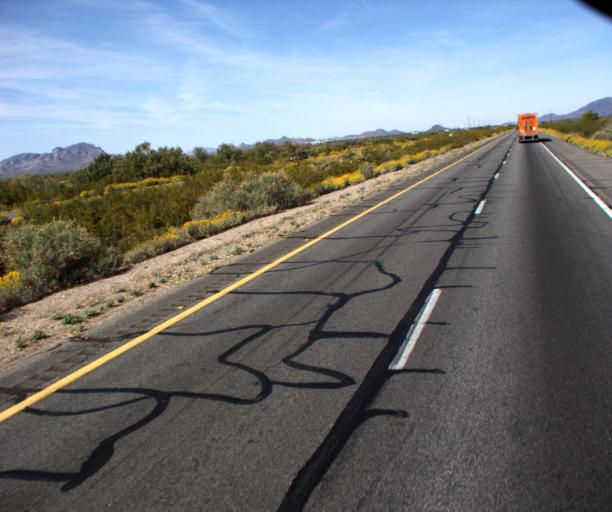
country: US
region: Arizona
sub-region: Maricopa County
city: Buckeye
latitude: 33.4910
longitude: -112.9076
